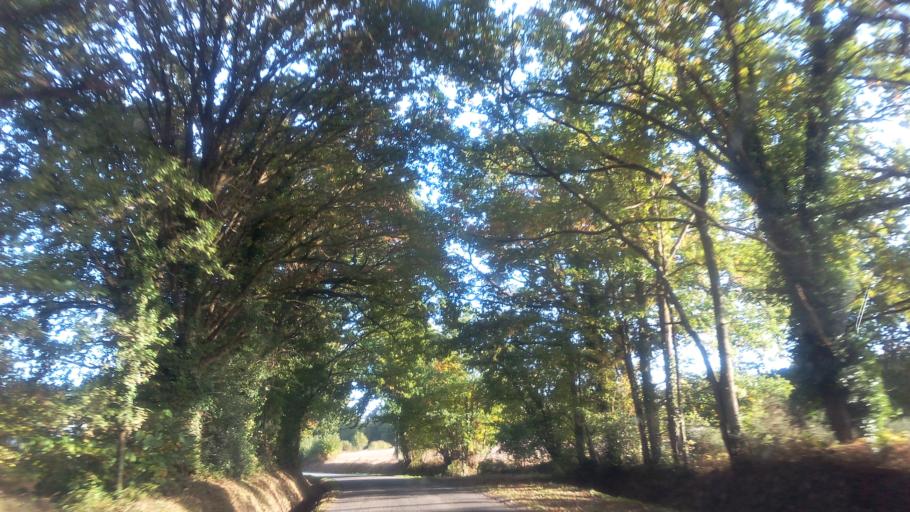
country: FR
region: Brittany
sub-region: Departement du Morbihan
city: Saint-Perreux
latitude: 47.6869
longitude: -2.0993
